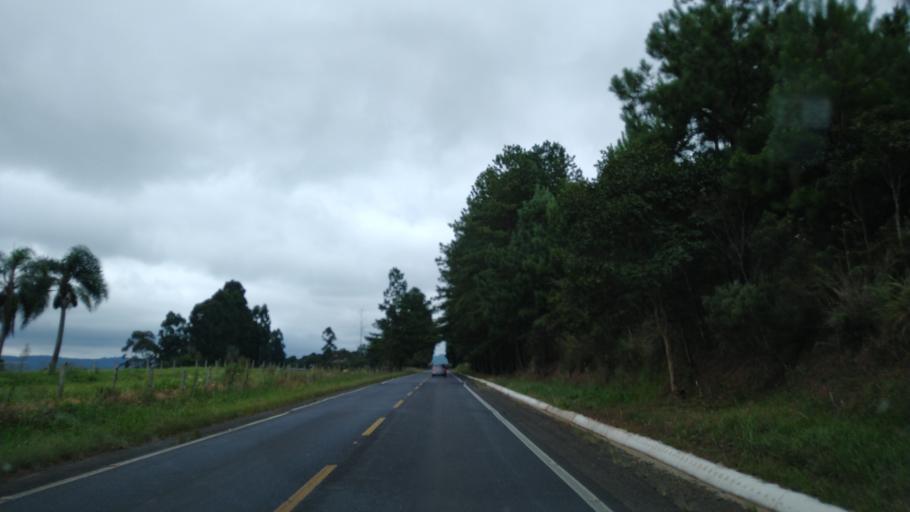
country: BR
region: Santa Catarina
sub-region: Porto Uniao
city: Porto Uniao
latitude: -26.2811
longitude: -50.9996
